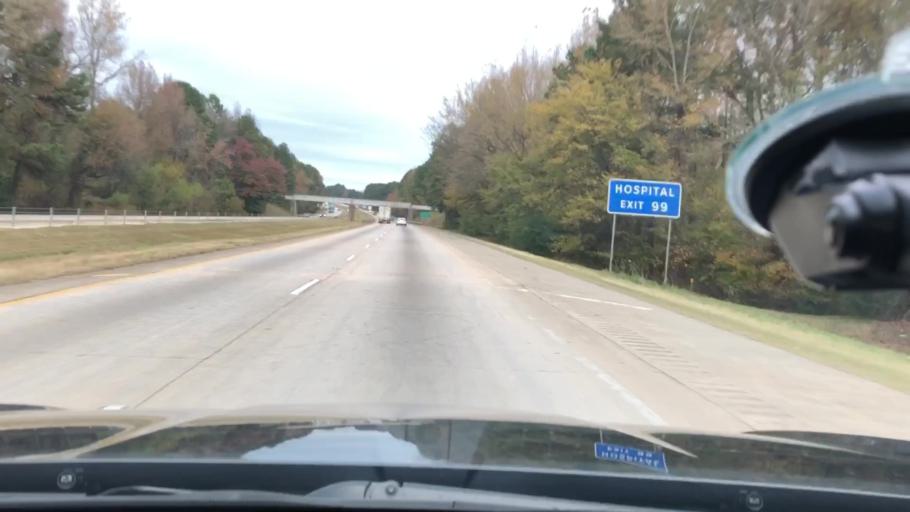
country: US
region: Arkansas
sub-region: Hot Spring County
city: Malvern
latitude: 34.4029
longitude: -92.8174
